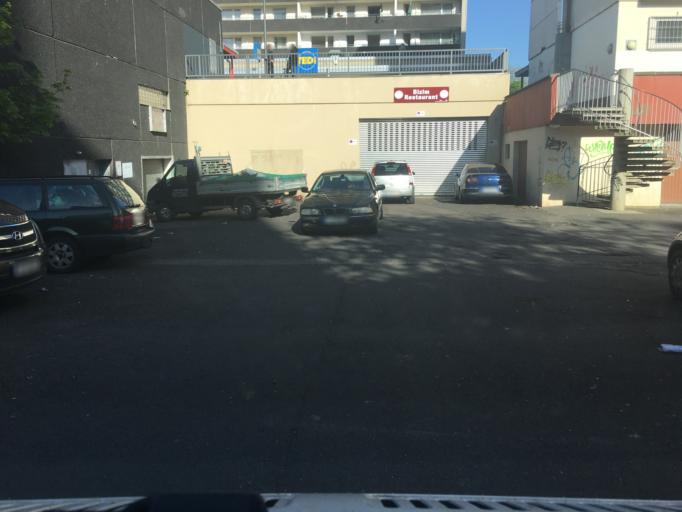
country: DE
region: North Rhine-Westphalia
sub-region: Regierungsbezirk Koln
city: Gremberghoven
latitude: 50.8963
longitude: 7.0634
